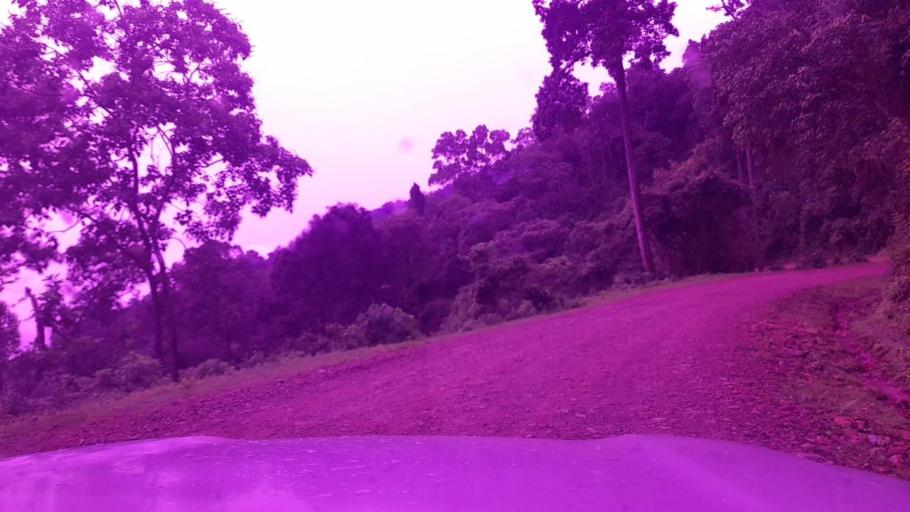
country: ET
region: Southern Nations, Nationalities, and People's Region
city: Bonga
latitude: 7.5080
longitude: 36.0632
